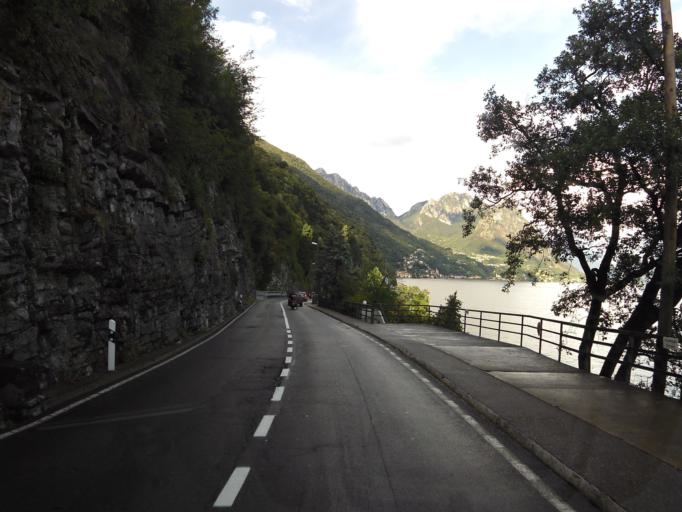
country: IT
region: Lombardy
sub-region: Provincia di Como
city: Lanzo d'Intelvi
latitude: 46.0099
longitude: 9.0103
